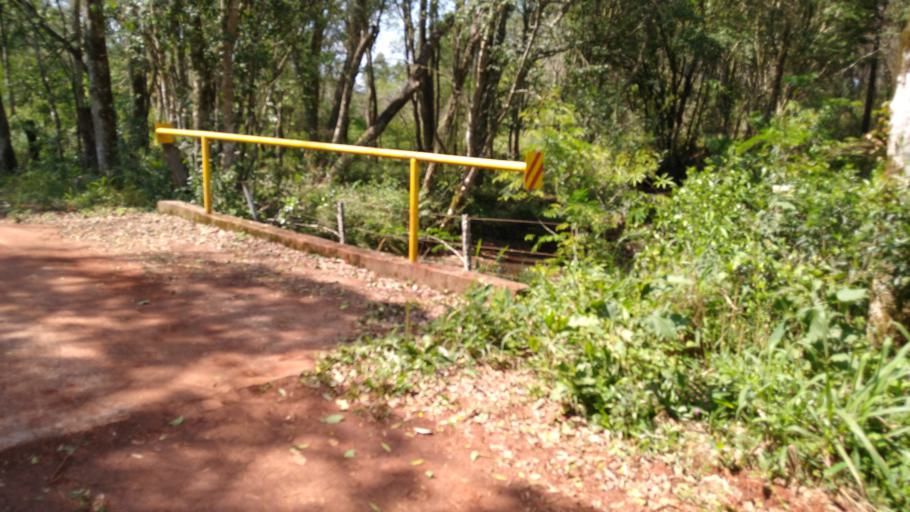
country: AR
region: Misiones
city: Capiovi
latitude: -26.9439
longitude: -55.0482
